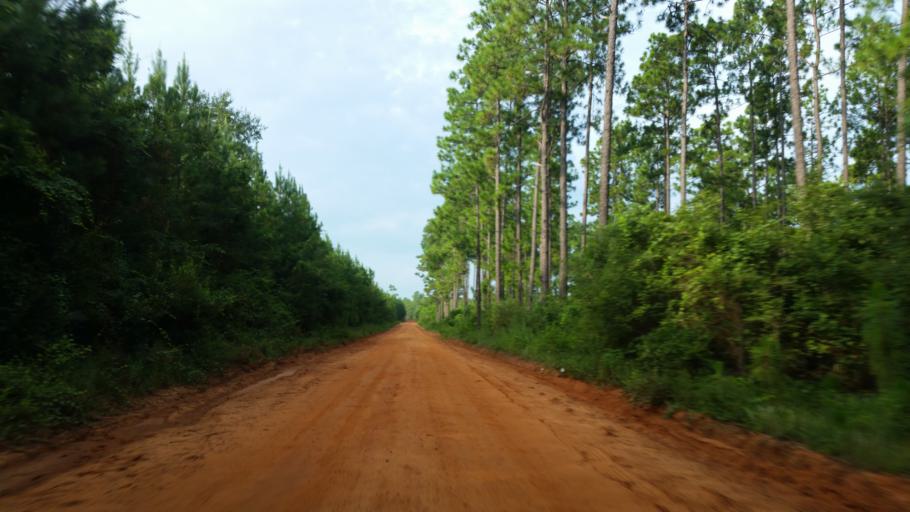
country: US
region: Alabama
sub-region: Escambia County
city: Atmore
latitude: 30.9134
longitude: -87.5802
